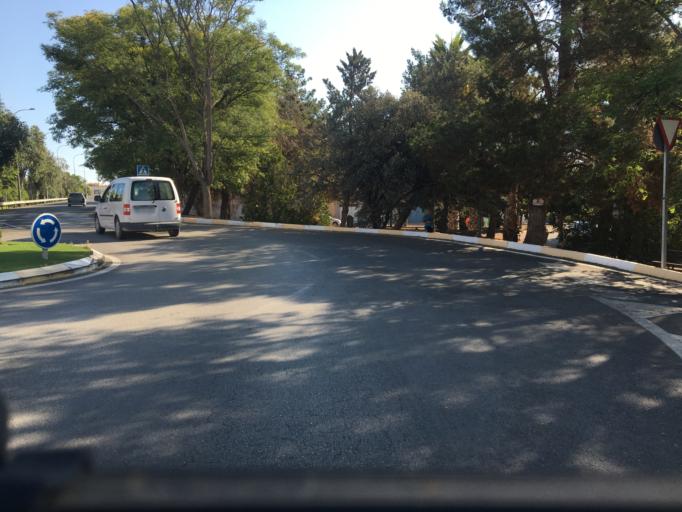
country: ES
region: Murcia
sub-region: Murcia
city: Puerto Lumbreras
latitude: 37.5577
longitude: -1.8095
